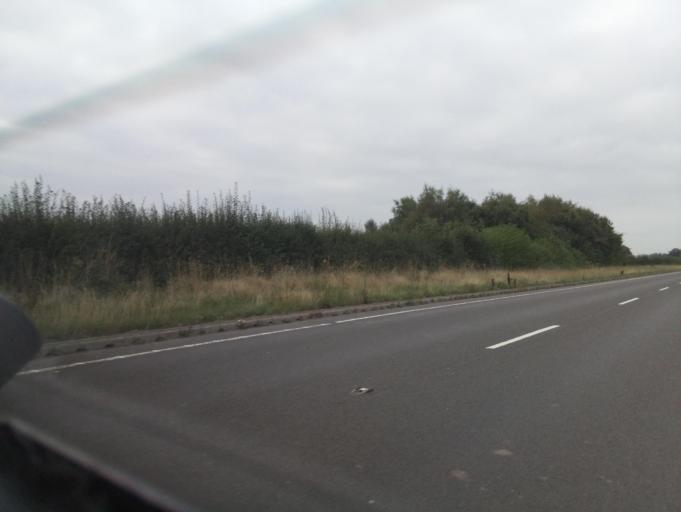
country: GB
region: England
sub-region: Shropshire
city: Stoke upon Tern
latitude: 52.8734
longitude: -2.5535
